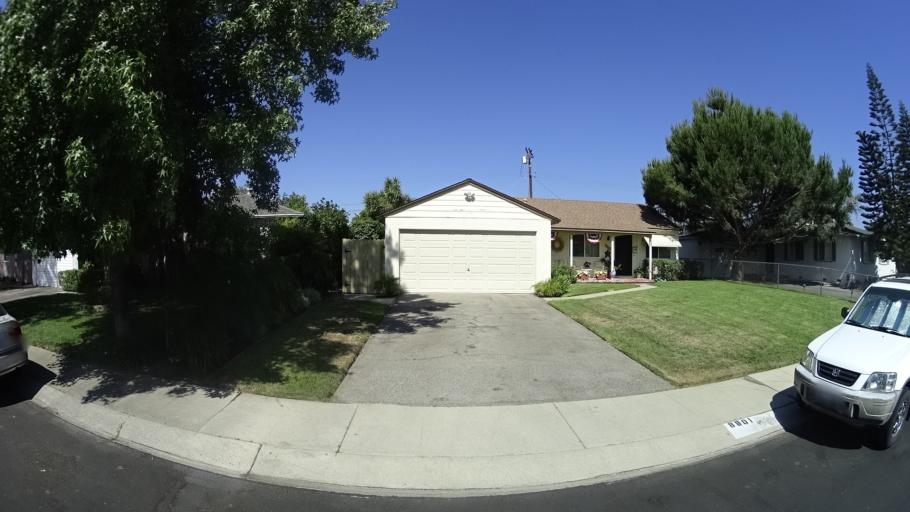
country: US
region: California
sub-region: Los Angeles County
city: Van Nuys
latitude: 34.2300
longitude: -118.4465
